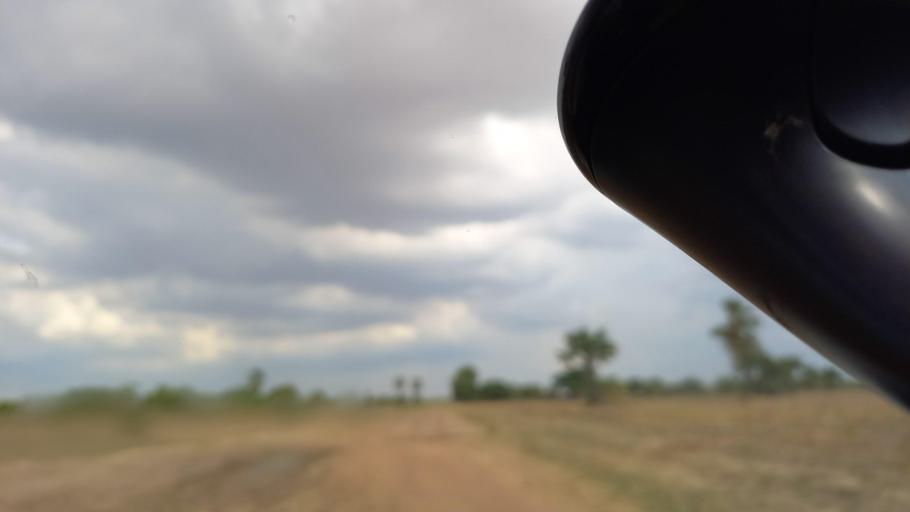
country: ZM
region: Lusaka
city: Kafue
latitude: -15.8372
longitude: 28.0830
